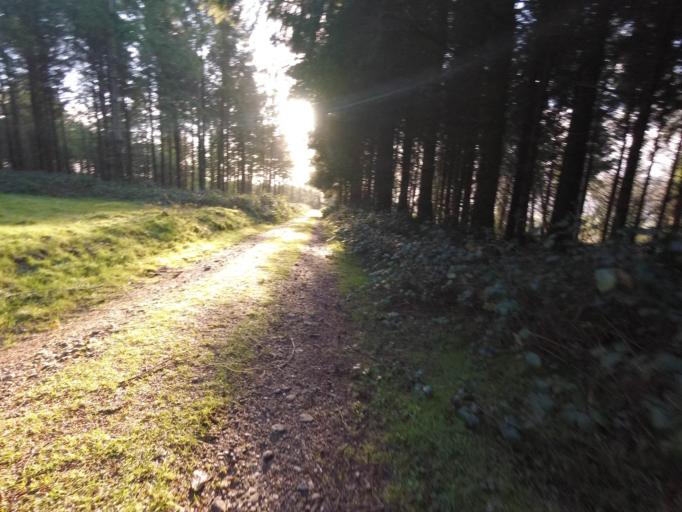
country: IE
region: Munster
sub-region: Waterford
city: Portlaw
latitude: 52.3094
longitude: -7.3558
